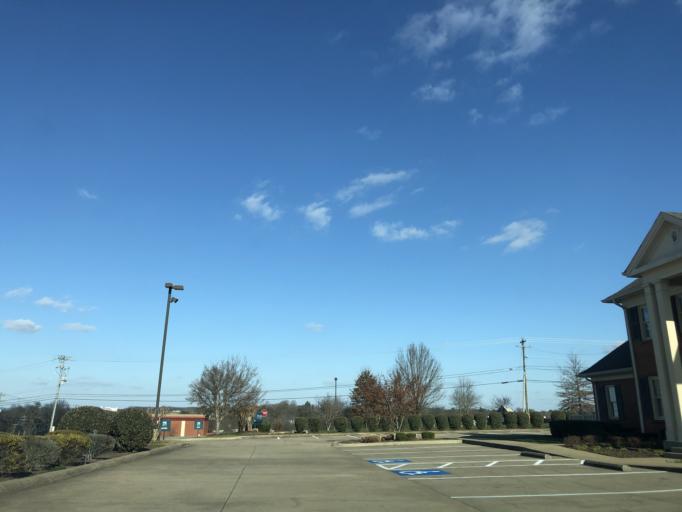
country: US
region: Tennessee
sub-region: Sumner County
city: Gallatin
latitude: 36.3650
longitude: -86.4899
